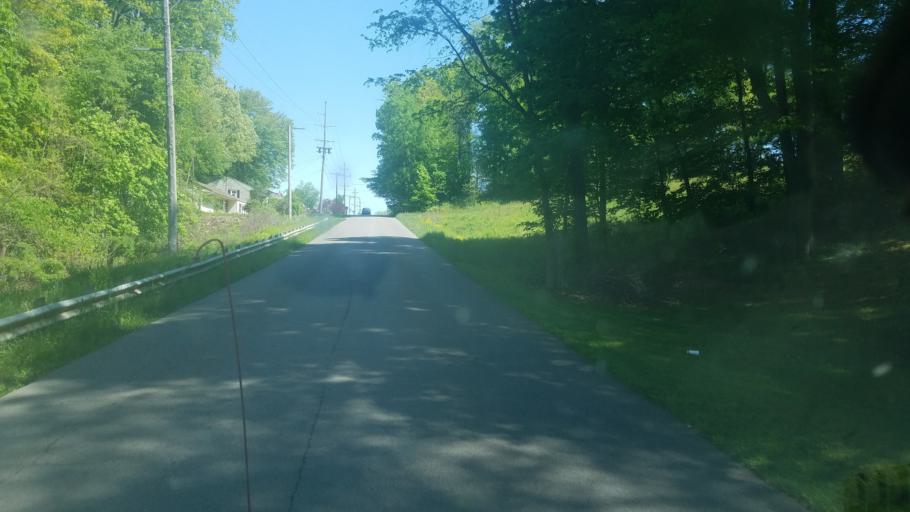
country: US
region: Ohio
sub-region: Richland County
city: Lincoln Heights
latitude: 40.7671
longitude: -82.4842
